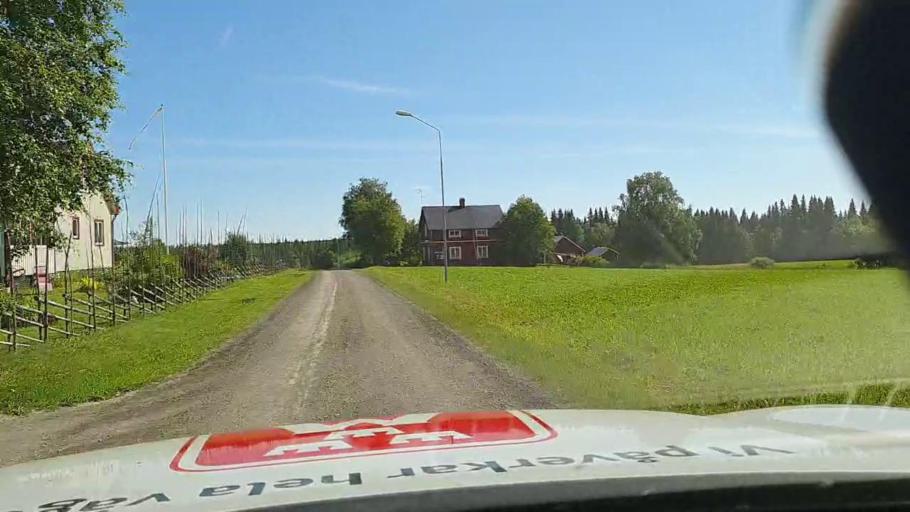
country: SE
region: Jaemtland
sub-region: Stroemsunds Kommun
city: Stroemsund
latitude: 63.7646
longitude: 15.3431
